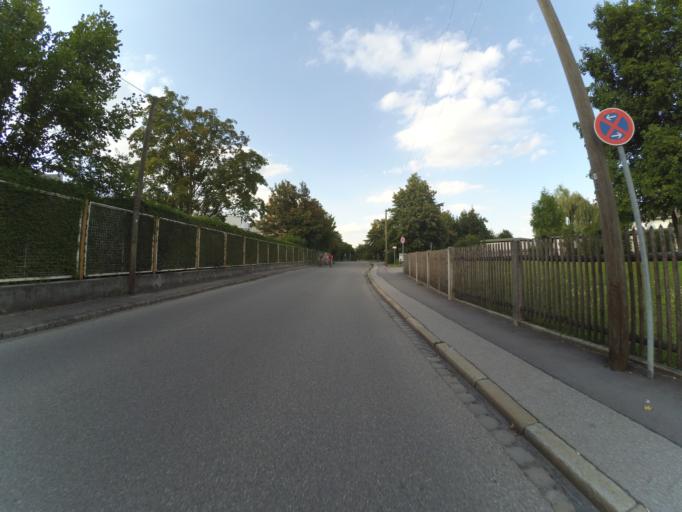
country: DE
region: Bavaria
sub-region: Upper Bavaria
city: Karlsfeld
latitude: 48.1920
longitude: 11.4736
